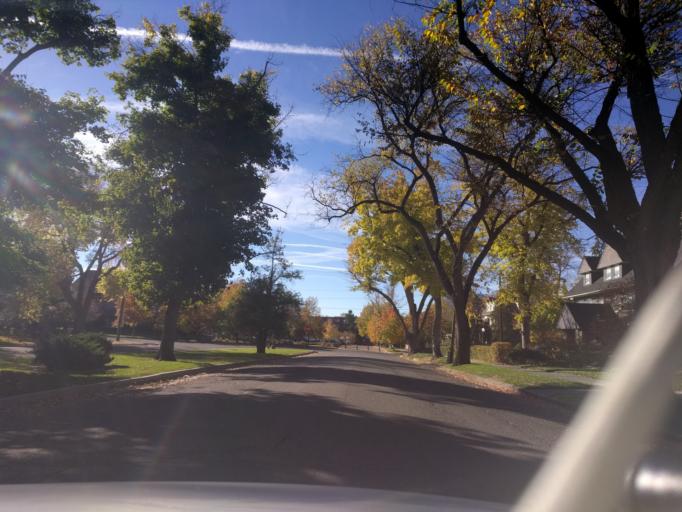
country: US
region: Colorado
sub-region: El Paso County
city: Colorado Springs
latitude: 38.8518
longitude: -104.8264
